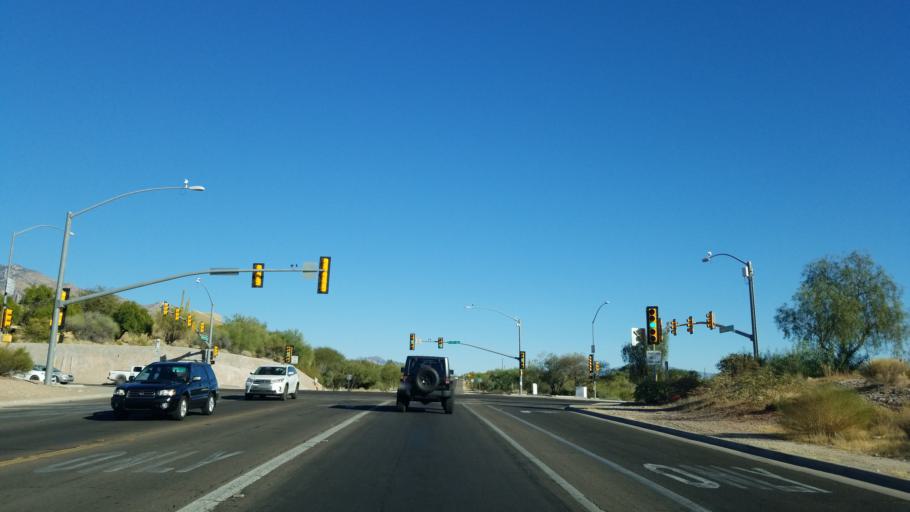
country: US
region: Arizona
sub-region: Pima County
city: Casas Adobes
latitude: 32.3229
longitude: -110.9616
